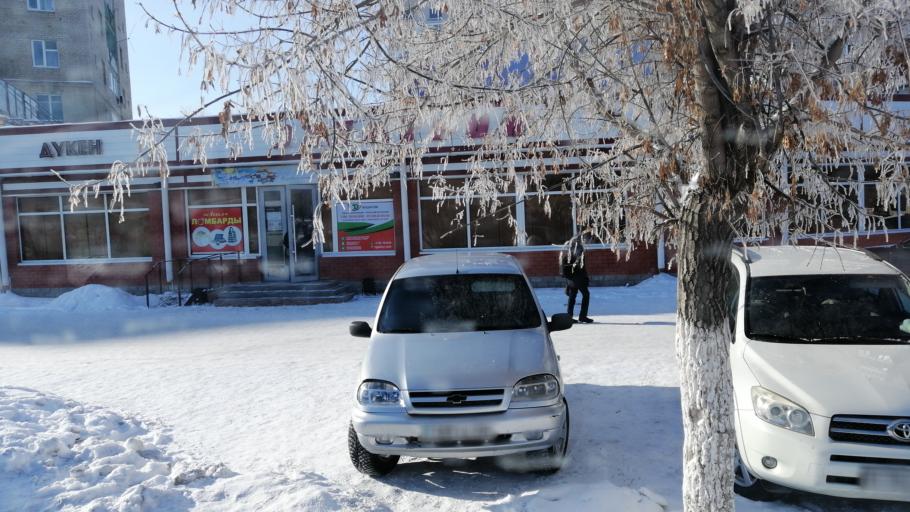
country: KZ
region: Aqtoebe
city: Aqtobe
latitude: 50.3030
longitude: 57.1525
